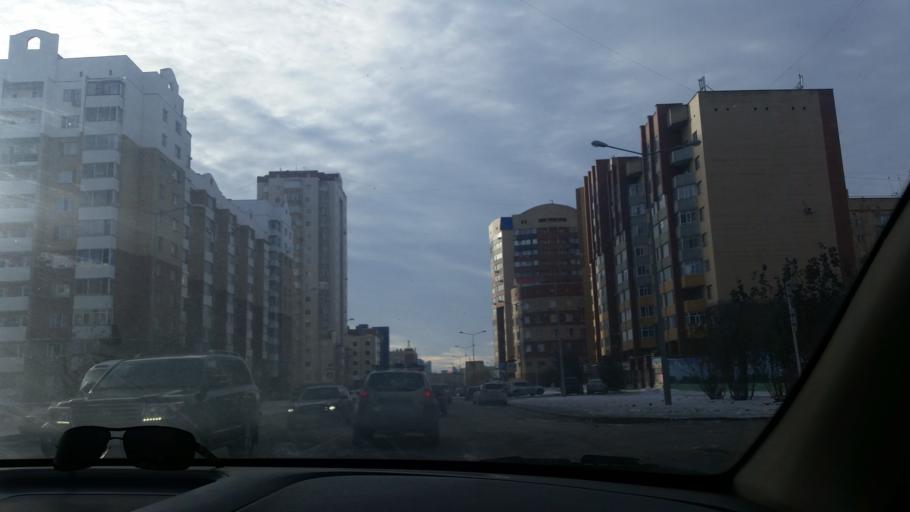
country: KZ
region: Astana Qalasy
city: Astana
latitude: 51.1485
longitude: 71.4795
